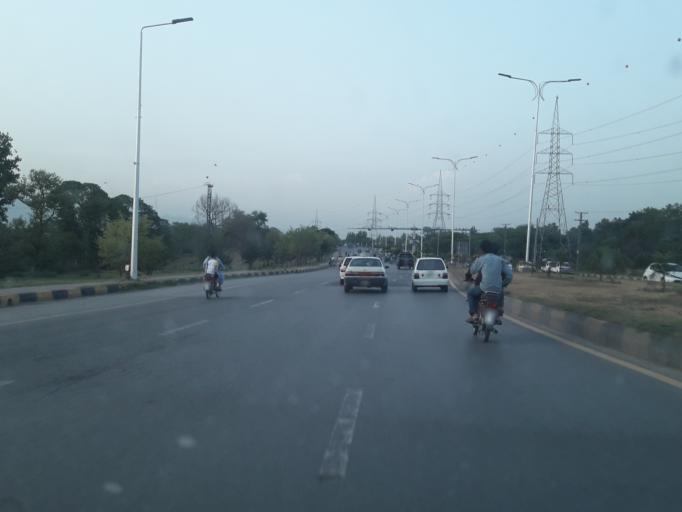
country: PK
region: Punjab
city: Rawalpindi
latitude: 33.6678
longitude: 73.0895
